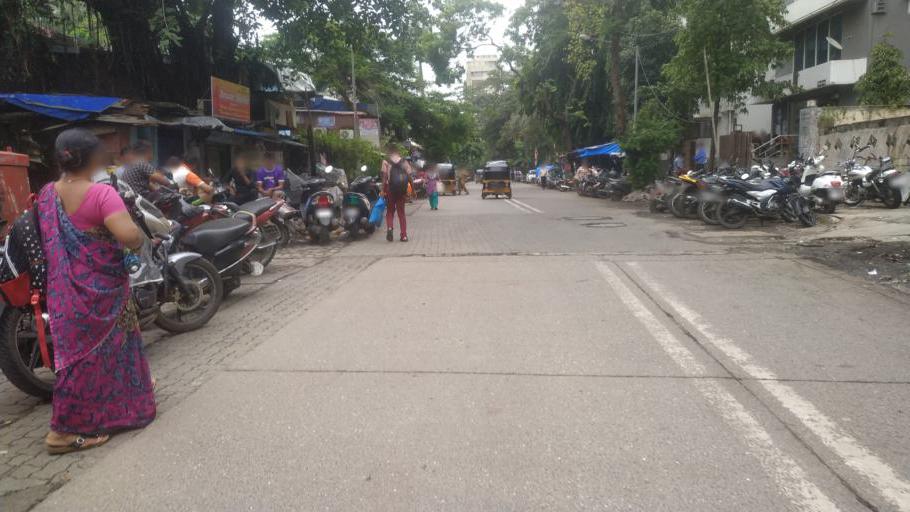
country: IN
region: Maharashtra
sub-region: Mumbai Suburban
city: Mumbai
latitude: 19.0669
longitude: 72.8300
